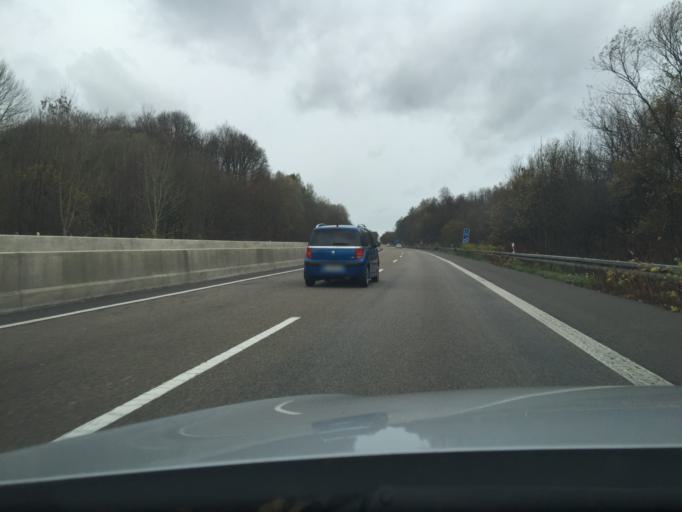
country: DE
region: North Rhine-Westphalia
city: Wulfrath
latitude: 51.2918
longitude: 7.0704
